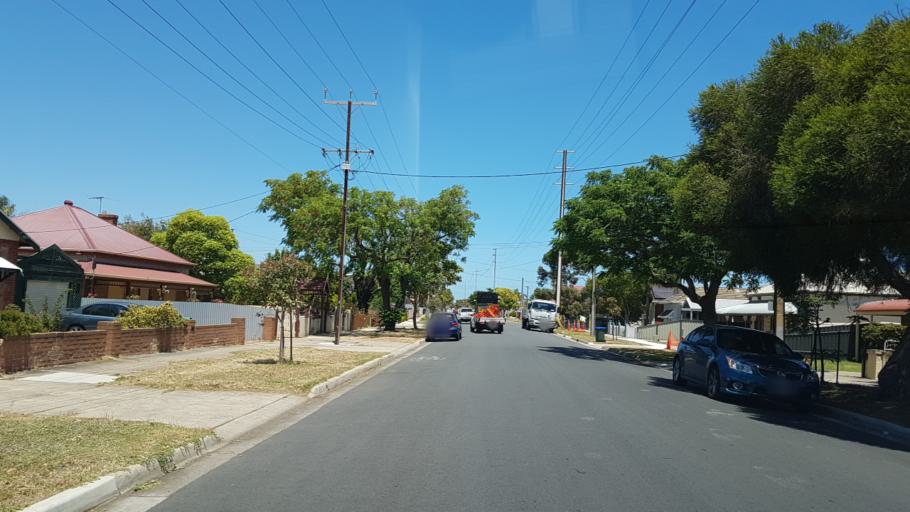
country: AU
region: South Australia
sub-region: Charles Sturt
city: West Lakes Shore
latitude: -34.8526
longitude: 138.4885
